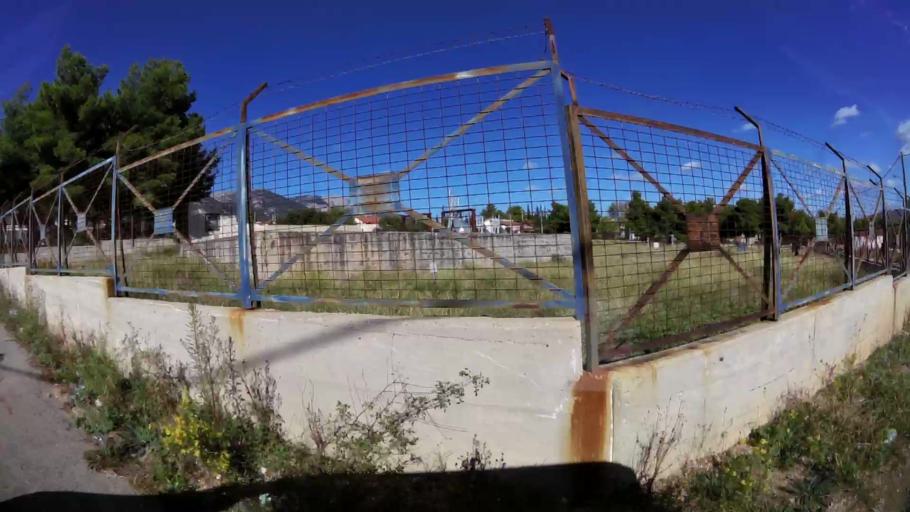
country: GR
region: Attica
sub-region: Nomarchia Anatolikis Attikis
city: Acharnes
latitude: 38.1030
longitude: 23.7223
